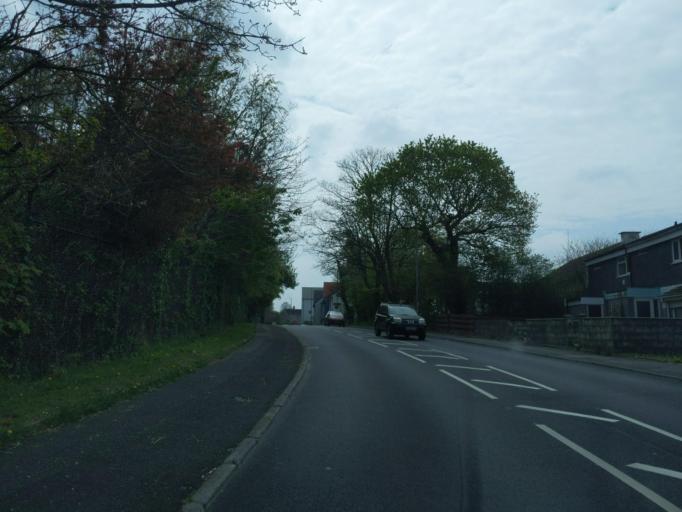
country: GB
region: England
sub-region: Plymouth
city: Plymouth
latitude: 50.4080
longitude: -4.1484
